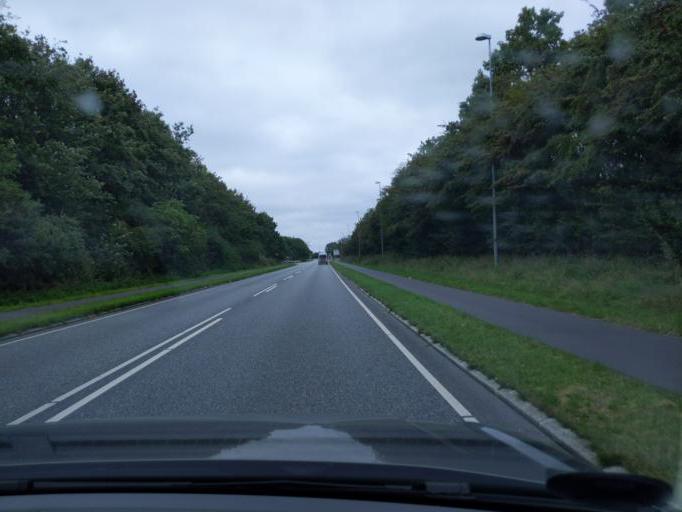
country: DK
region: Central Jutland
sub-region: Randers Kommune
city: Randers
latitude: 56.4844
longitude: 9.9924
